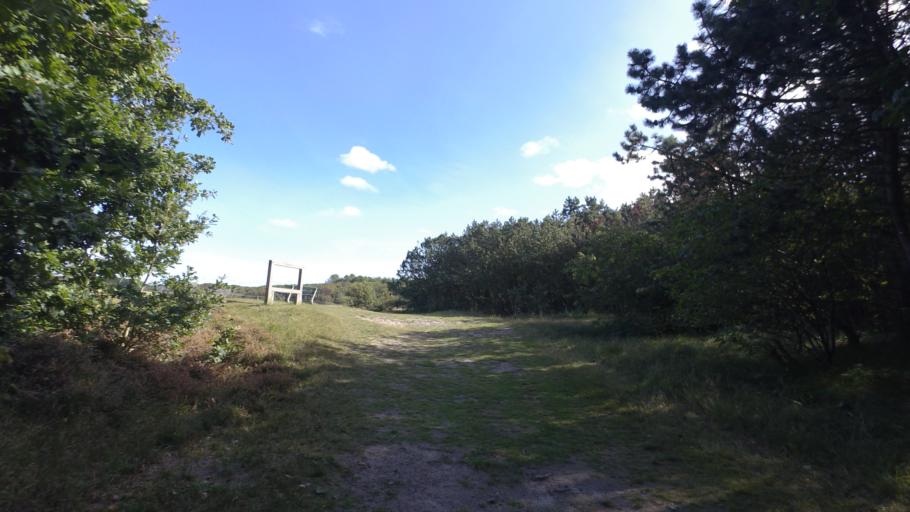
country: NL
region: Friesland
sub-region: Gemeente Ameland
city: Hollum
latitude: 53.4495
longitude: 5.7007
